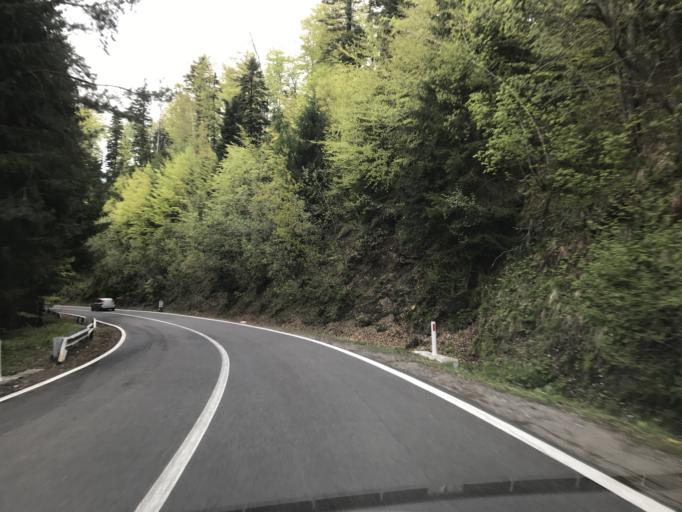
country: RO
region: Sibiu
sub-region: Comuna Cartisoara
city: Cartisoara
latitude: 45.6611
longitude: 24.5970
